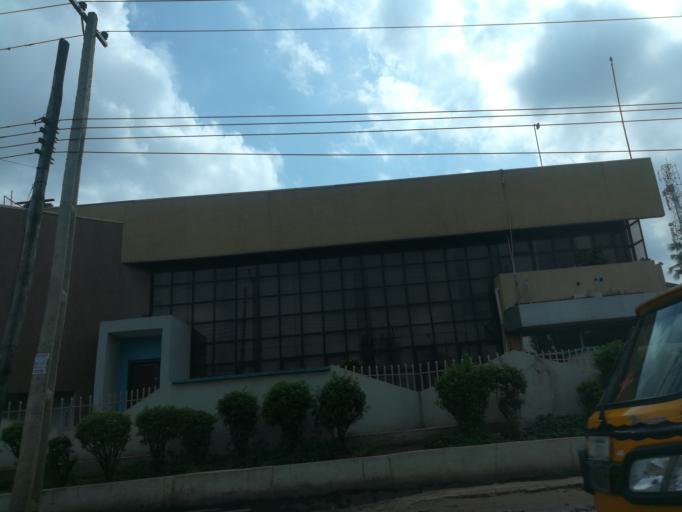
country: NG
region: Lagos
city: Oshodi
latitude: 6.5521
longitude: 3.3554
